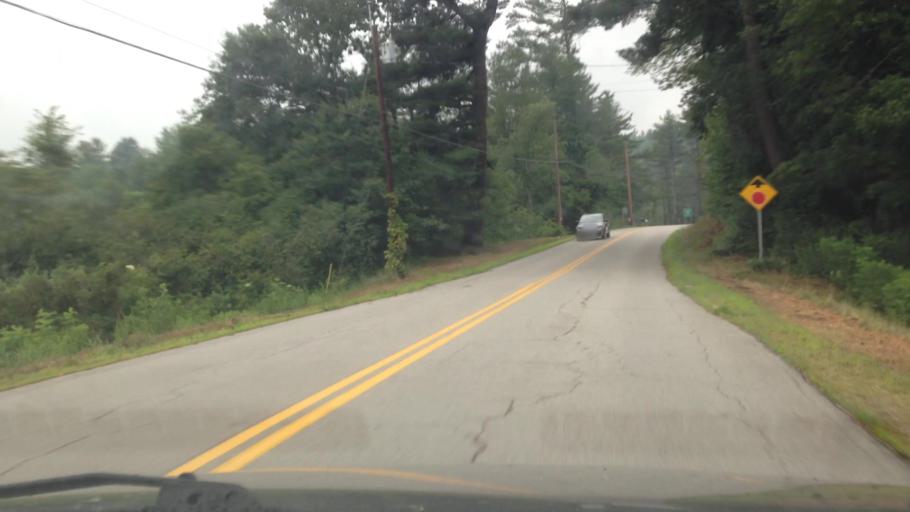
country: US
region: New Hampshire
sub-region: Cheshire County
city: Swanzey
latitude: 42.8444
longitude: -72.2767
